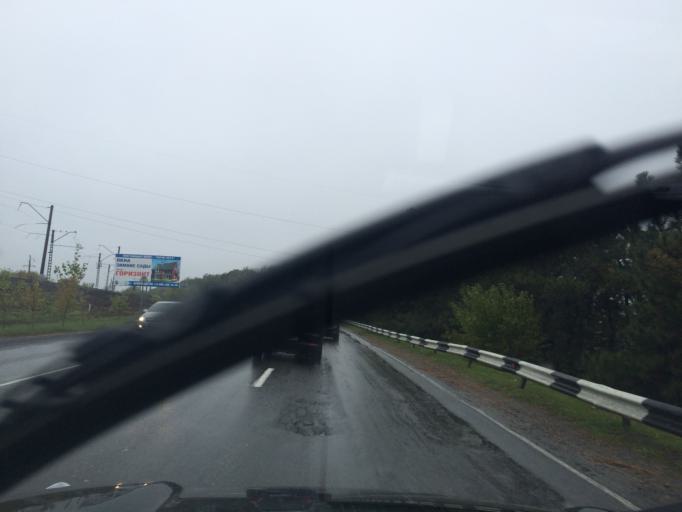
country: RU
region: Rostov
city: Azov
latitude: 47.0854
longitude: 39.4722
